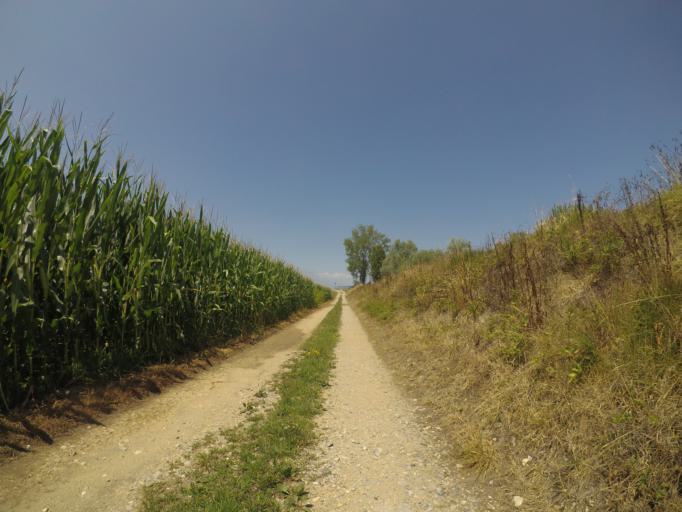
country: IT
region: Friuli Venezia Giulia
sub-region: Provincia di Udine
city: Codroipo
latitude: 45.9296
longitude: 13.0081
